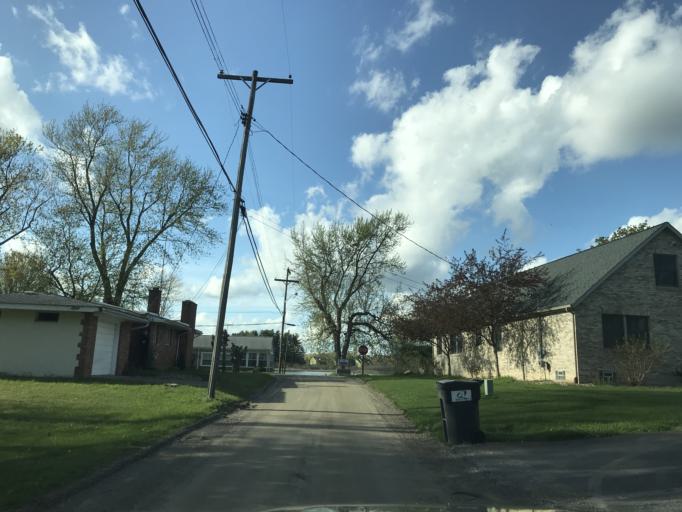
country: US
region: Michigan
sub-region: Livingston County
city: Brighton
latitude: 42.5438
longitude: -83.7546
